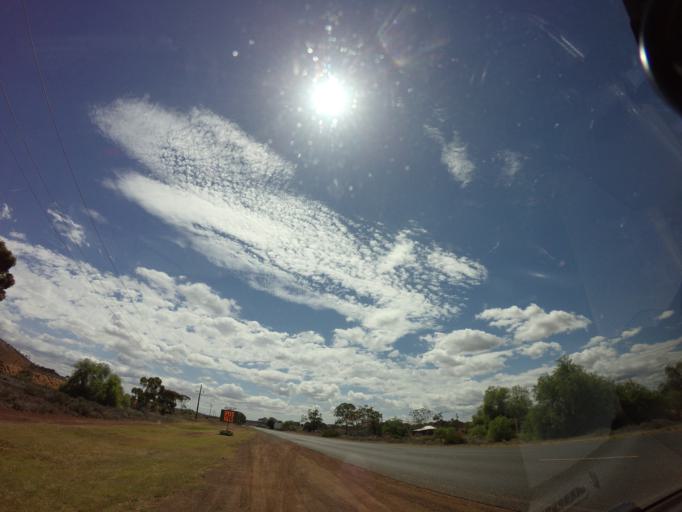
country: AU
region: Western Australia
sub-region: Kalgoorlie/Boulder
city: Boulder
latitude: -30.9538
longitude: 121.1765
